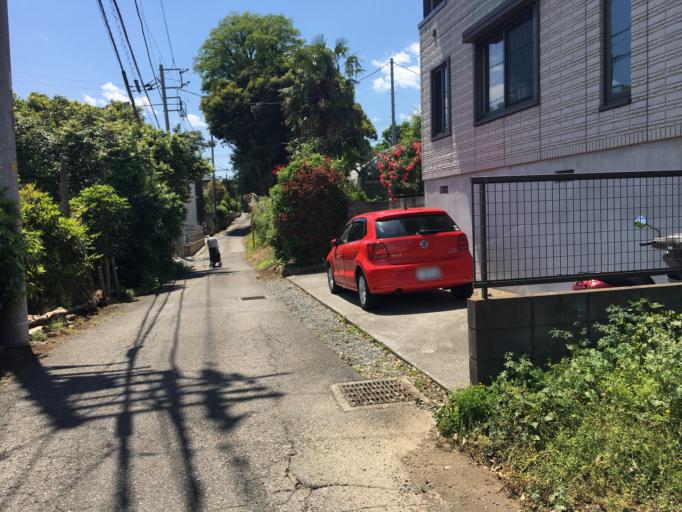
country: JP
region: Saitama
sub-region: Kawaguchi-shi
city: Hatogaya-honcho
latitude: 35.8472
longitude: 139.7484
